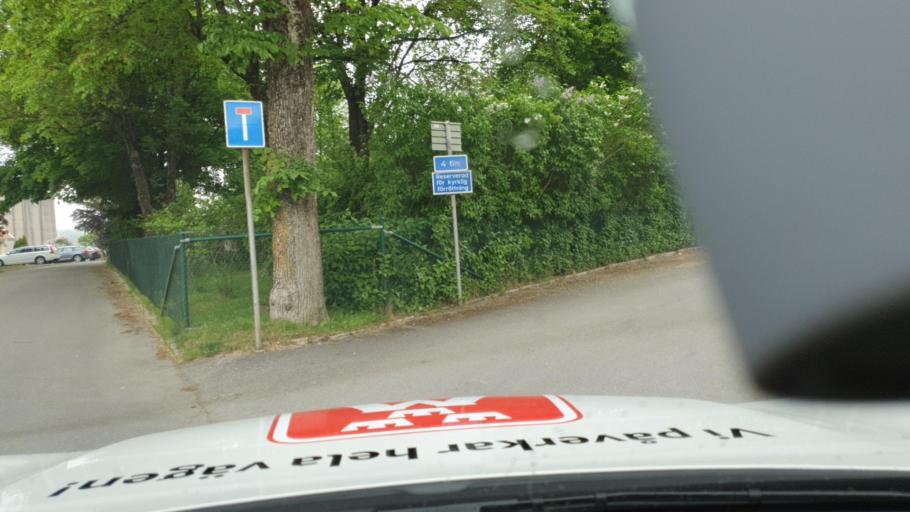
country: SE
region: Vaestra Goetaland
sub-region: Falkopings Kommun
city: Falkoeping
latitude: 58.1602
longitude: 13.5503
